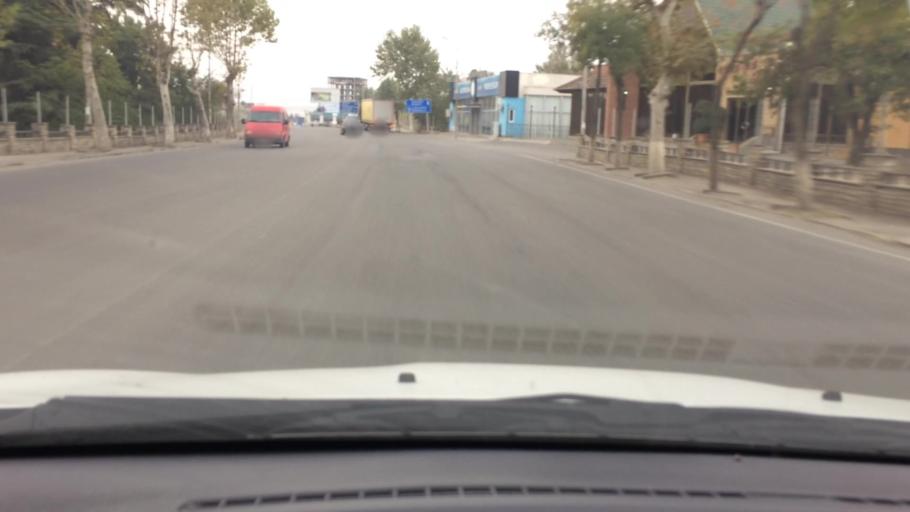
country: GE
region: Kvemo Kartli
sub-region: Marneuli
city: Marneuli
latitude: 41.4893
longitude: 44.7996
